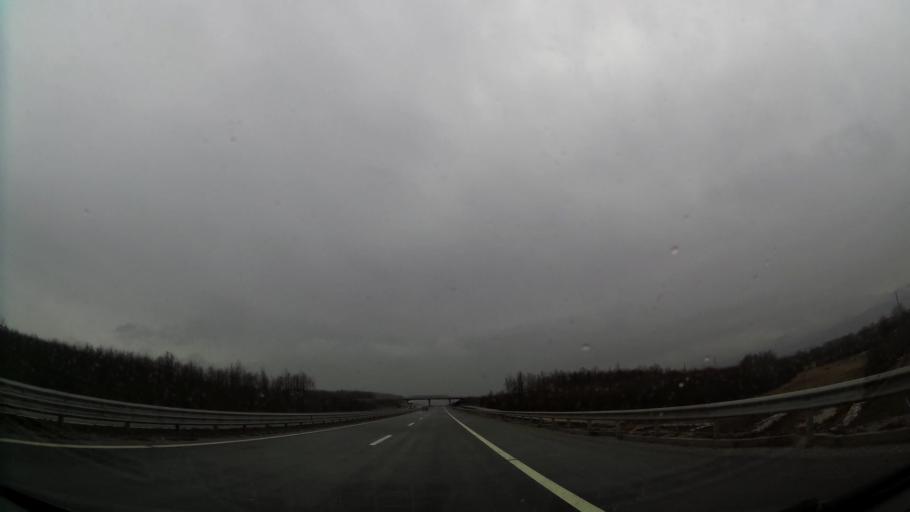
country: XK
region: Ferizaj
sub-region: Komuna e Ferizajt
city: Ferizaj
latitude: 42.3372
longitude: 21.2051
